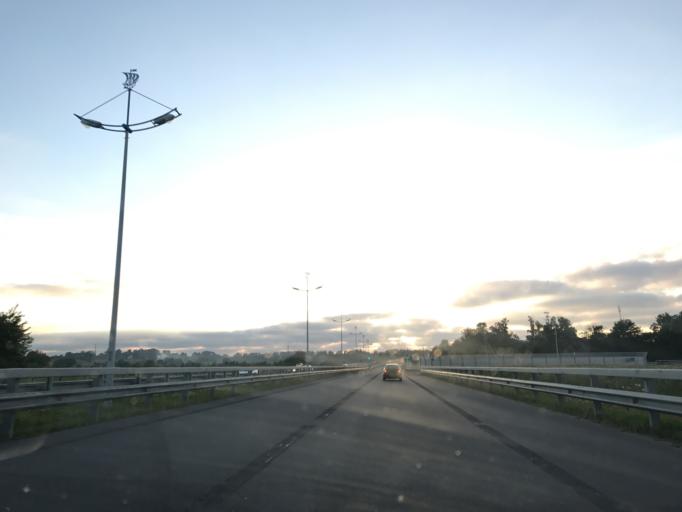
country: RU
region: Kaliningrad
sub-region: Gorod Kaliningrad
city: Pionerskiy
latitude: 54.9152
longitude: 20.1969
